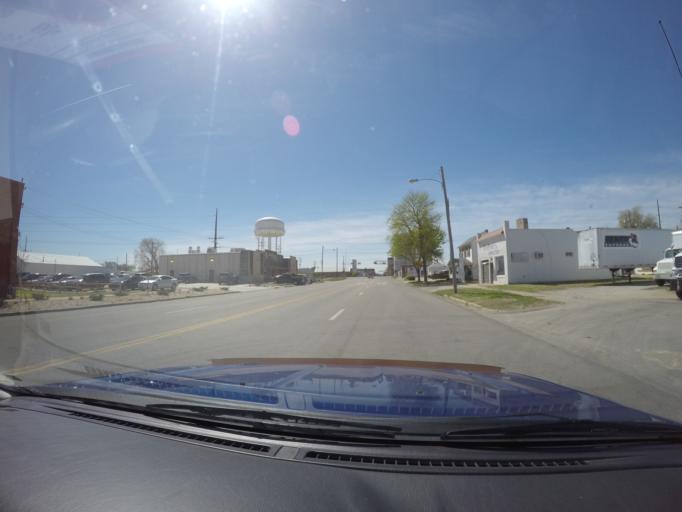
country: US
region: Kansas
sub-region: Saline County
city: Salina
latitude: 38.8514
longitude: -97.6091
